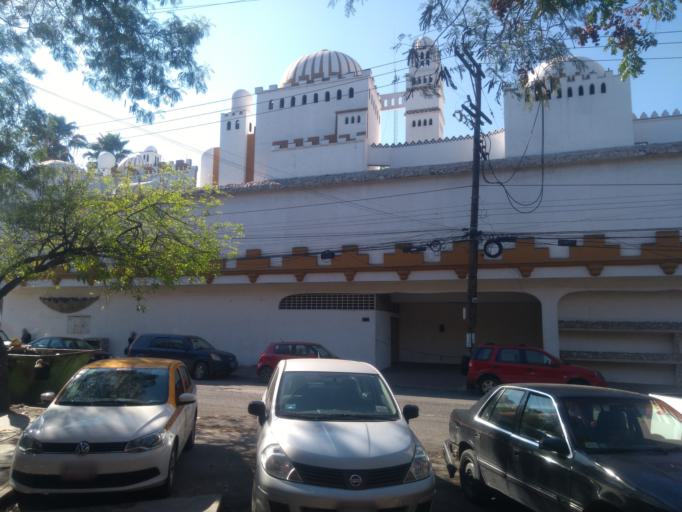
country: MX
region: Nuevo Leon
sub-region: Monterrey
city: Monterrey
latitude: 25.6678
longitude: -100.3033
